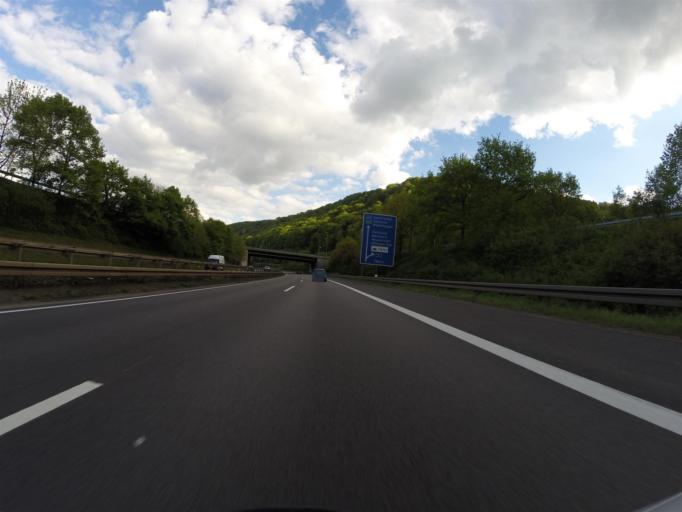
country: DE
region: Saarland
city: Wallerfangen
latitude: 49.3461
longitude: 6.7018
